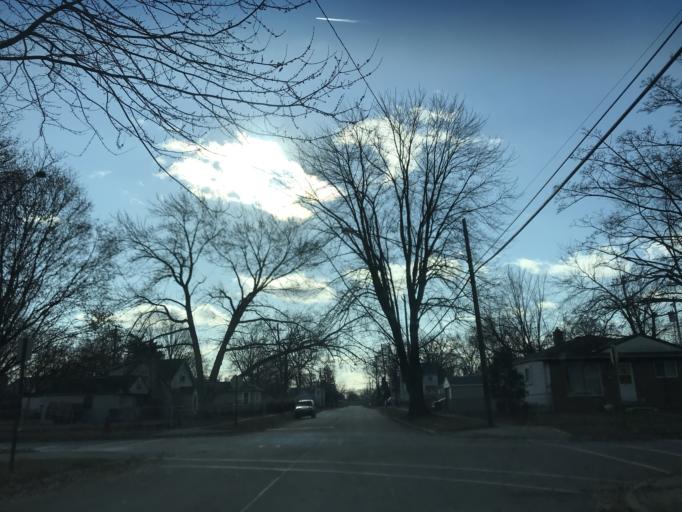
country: US
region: Michigan
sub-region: Oakland County
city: Hazel Park
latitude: 42.4513
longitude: -83.0933
